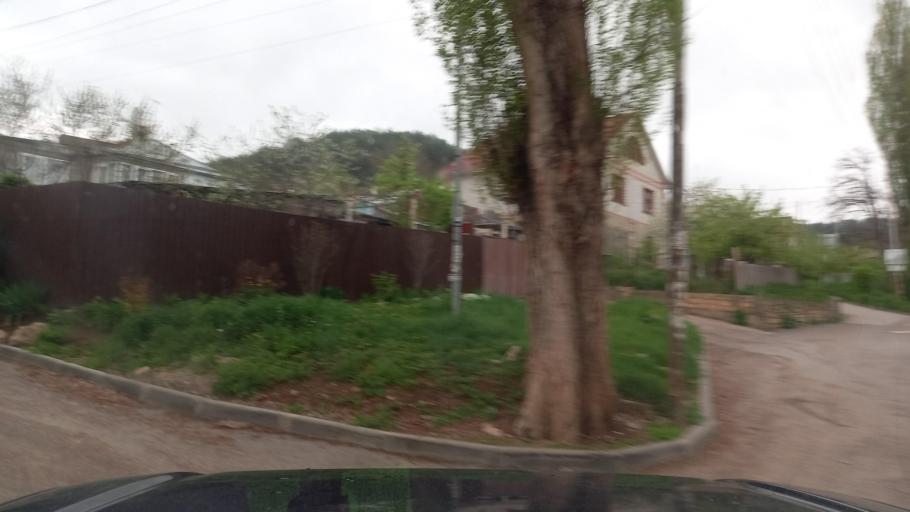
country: RU
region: Stavropol'skiy
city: Kislovodsk
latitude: 43.8900
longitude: 42.7006
